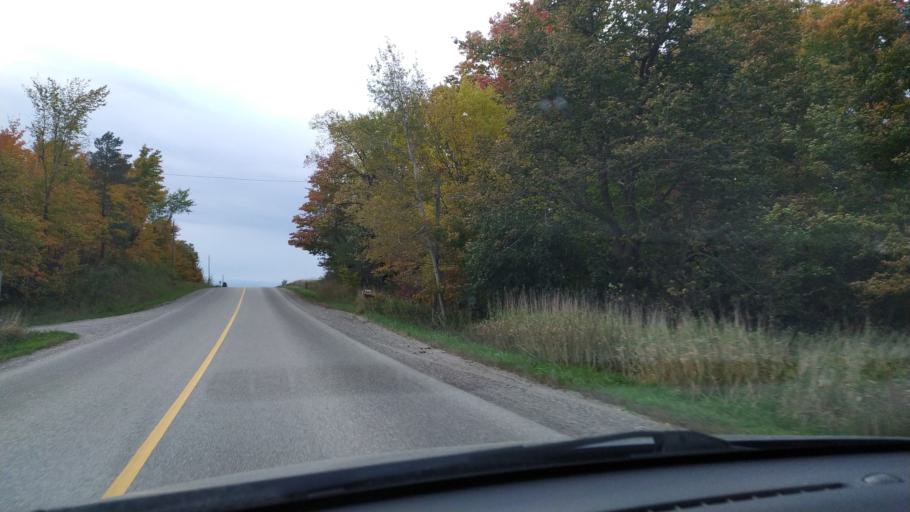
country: CA
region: Ontario
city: Waterloo
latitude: 43.5092
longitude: -80.7064
